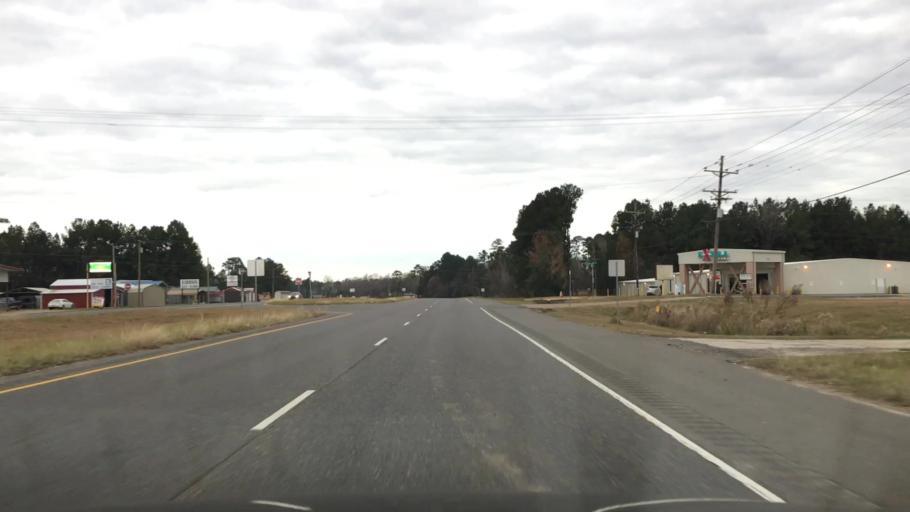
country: US
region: Louisiana
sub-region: Vernon Parish
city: New Llano
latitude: 31.0735
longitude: -93.2738
